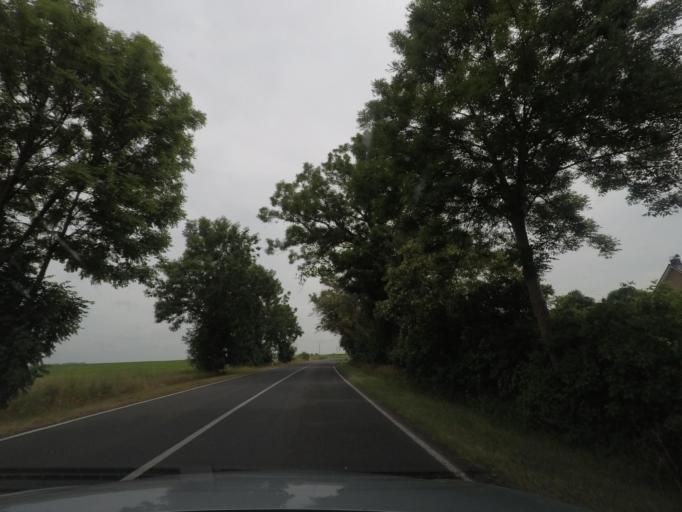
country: DE
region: Saxony-Anhalt
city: Klein Wanzleben
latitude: 52.0349
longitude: 11.3902
